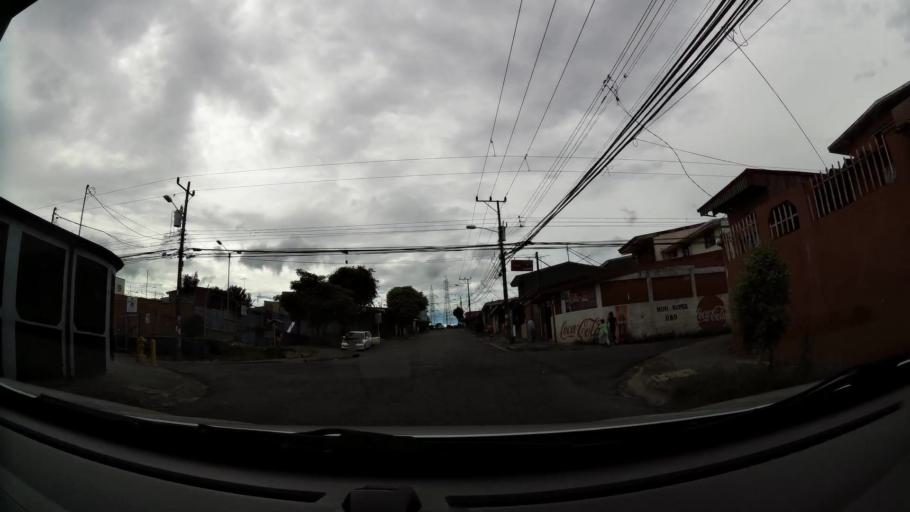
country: CR
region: San Jose
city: Purral
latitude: 9.9638
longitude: -84.0233
